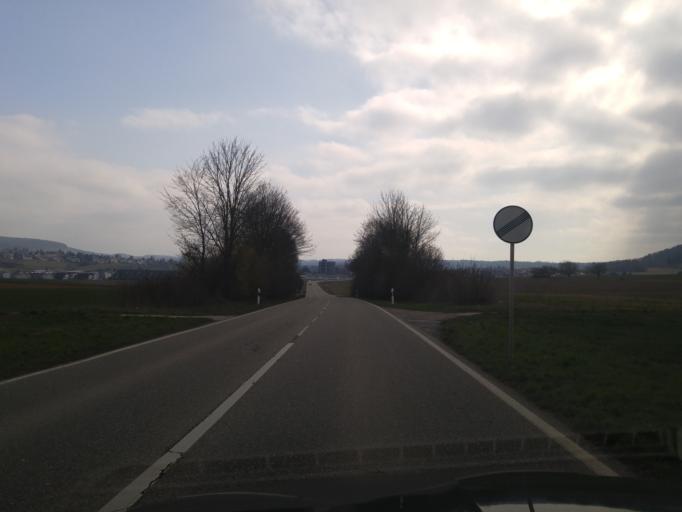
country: DE
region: Baden-Wuerttemberg
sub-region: Regierungsbezirk Stuttgart
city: Flein
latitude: 49.1071
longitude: 9.1911
